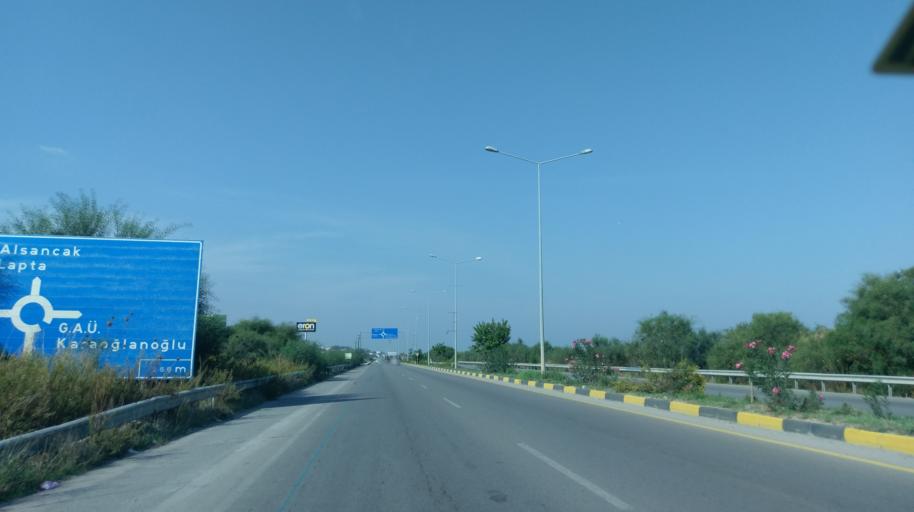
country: CY
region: Keryneia
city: Kyrenia
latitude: 35.3298
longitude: 33.2792
